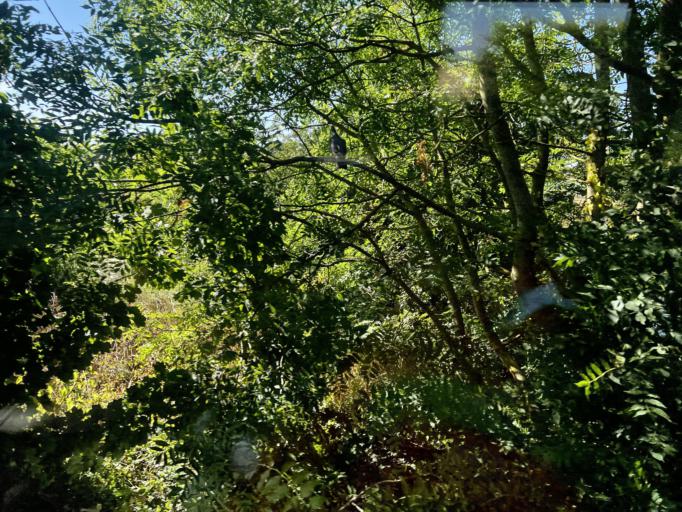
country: GB
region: England
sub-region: Lincolnshire
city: Donington
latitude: 52.9741
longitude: -0.1515
